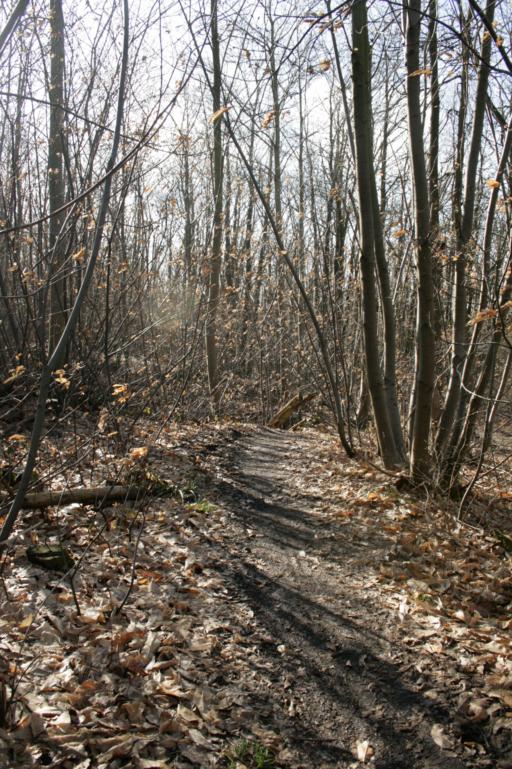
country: FR
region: Ile-de-France
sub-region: Departement des Yvelines
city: Vaux-sur-Seine
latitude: 49.0118
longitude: 1.9851
